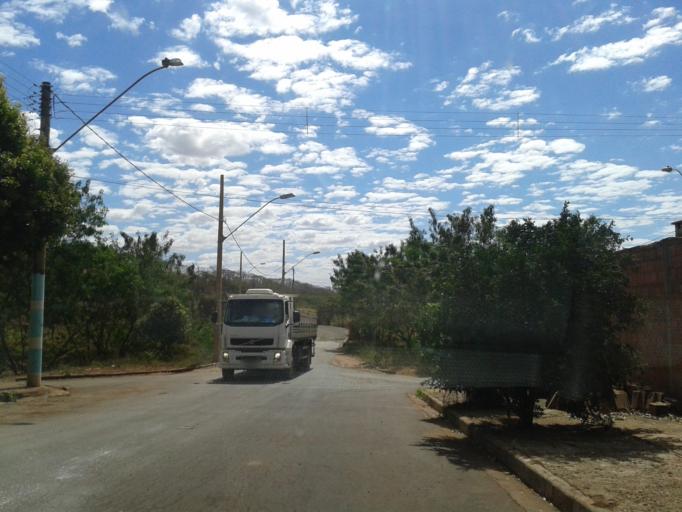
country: BR
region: Minas Gerais
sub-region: Ituiutaba
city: Ituiutaba
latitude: -18.9605
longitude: -49.4703
